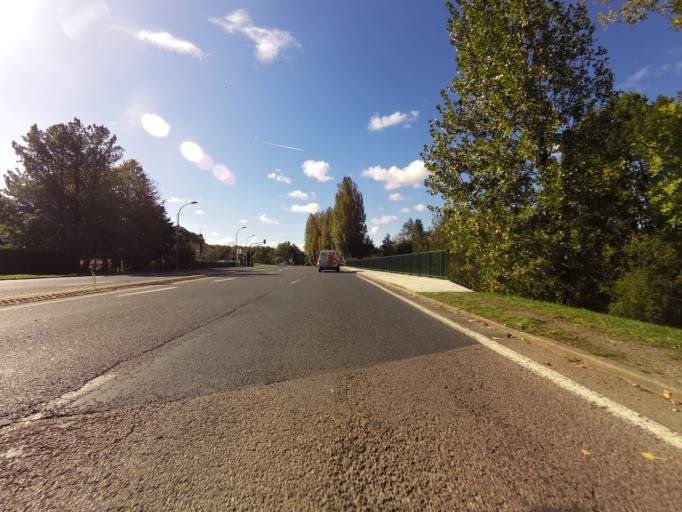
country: FR
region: Lower Normandy
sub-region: Departement du Calvados
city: Saint-Pierre-sur-Dives
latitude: 49.0221
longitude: -0.0365
